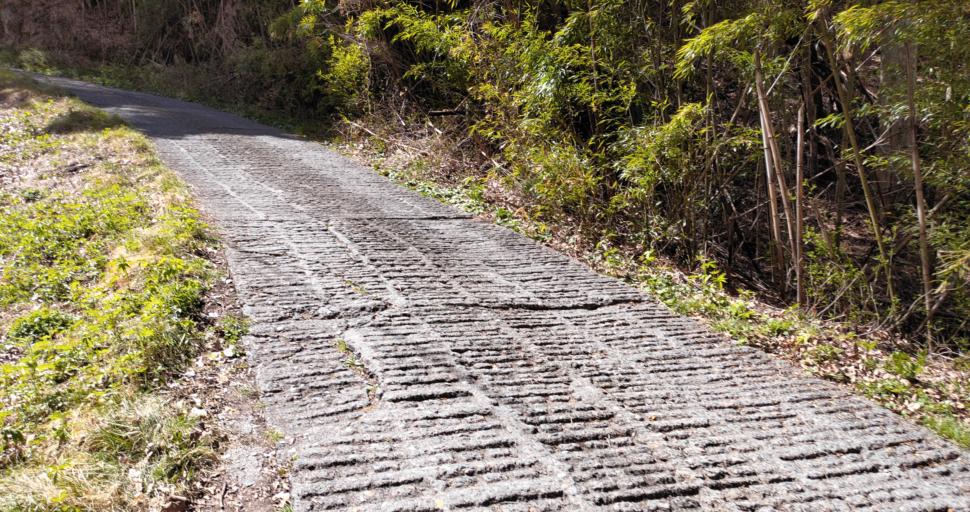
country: JP
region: Nagano
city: Komoro
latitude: 36.3291
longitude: 138.3849
